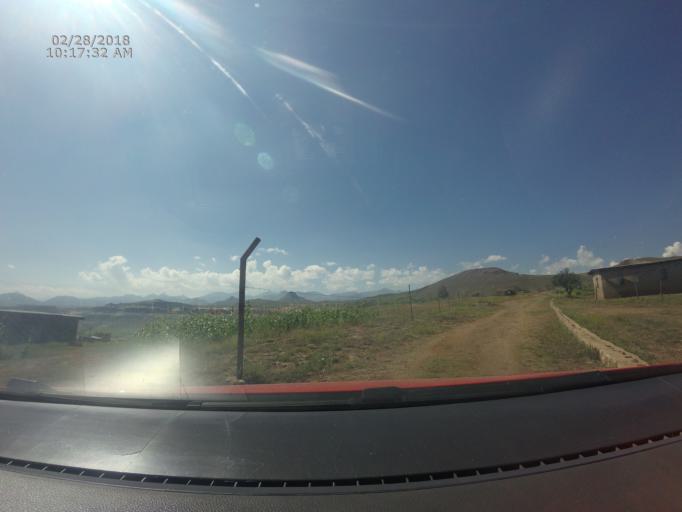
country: LS
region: Berea
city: Teyateyaneng
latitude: -29.2233
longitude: 27.8689
